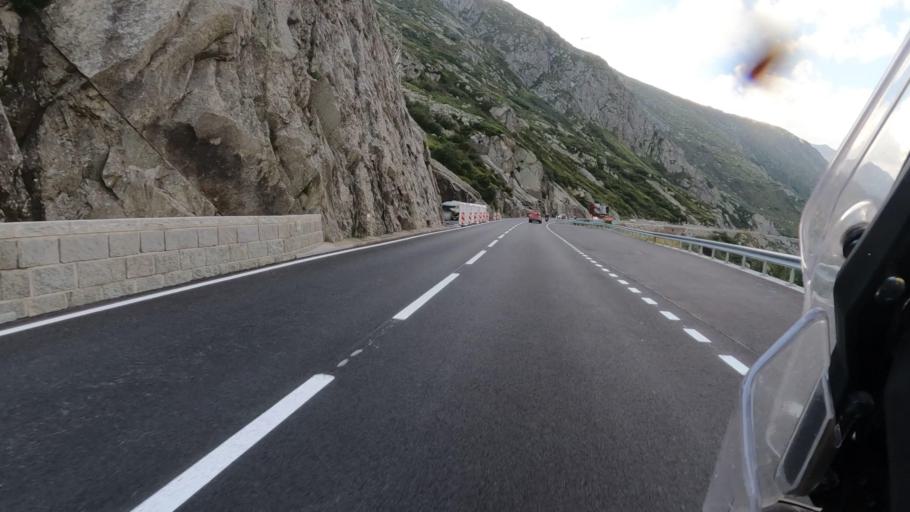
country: CH
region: Uri
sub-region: Uri
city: Andermatt
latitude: 46.5830
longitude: 8.5585
